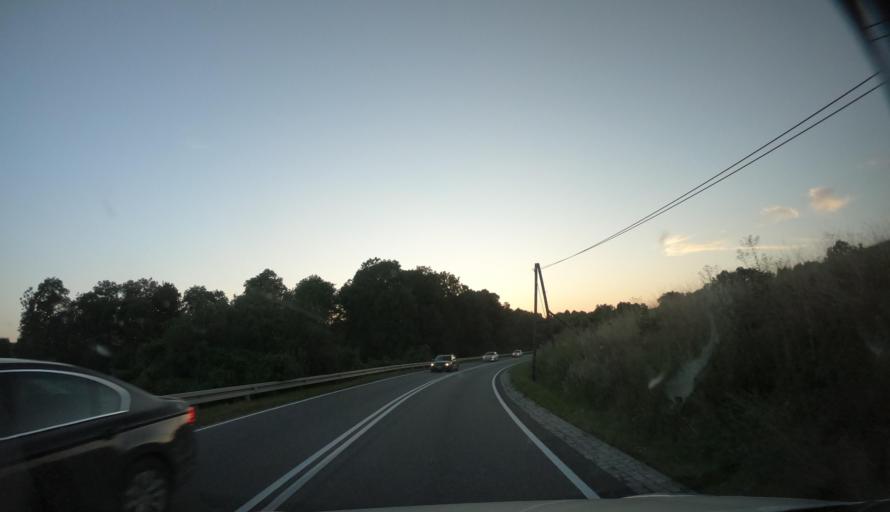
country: PL
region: Kujawsko-Pomorskie
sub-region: Powiat bydgoski
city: Koronowo
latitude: 53.3568
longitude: 17.8639
